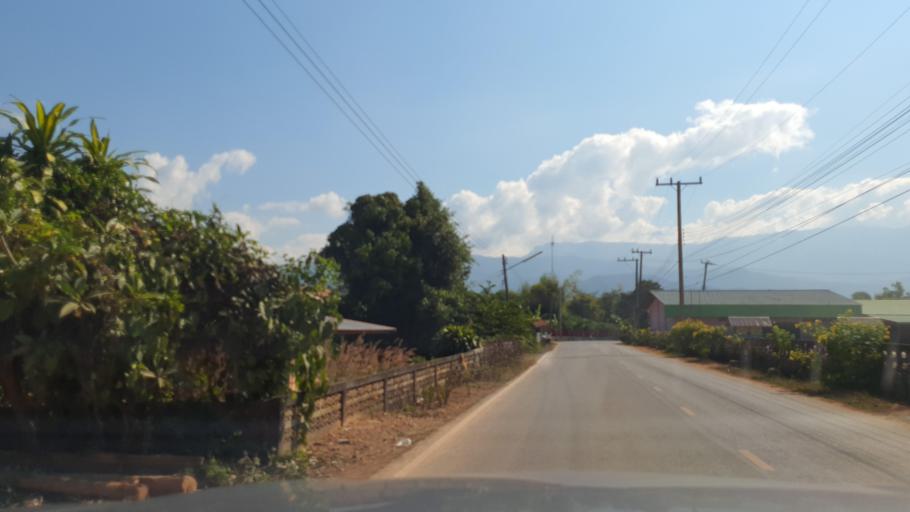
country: TH
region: Nan
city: Pua
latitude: 19.1441
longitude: 100.9236
